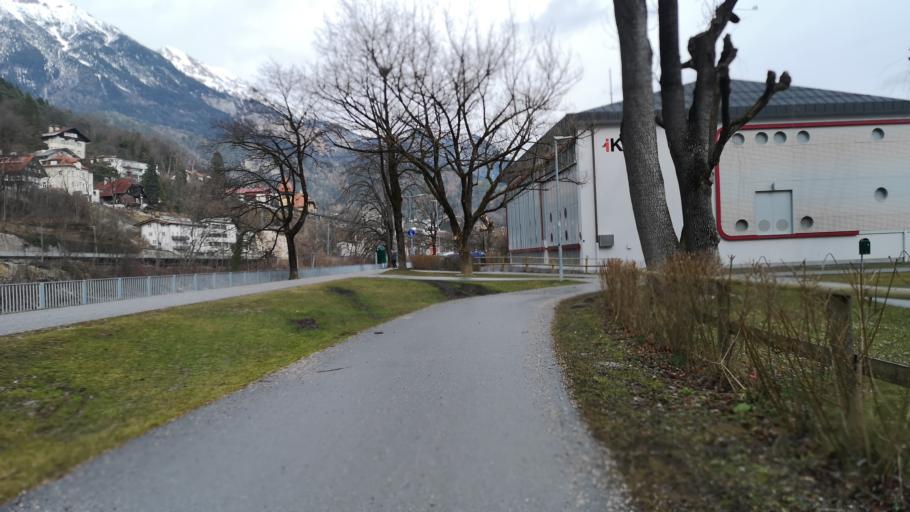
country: AT
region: Tyrol
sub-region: Innsbruck Stadt
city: Innsbruck
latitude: 47.2784
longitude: 11.4010
